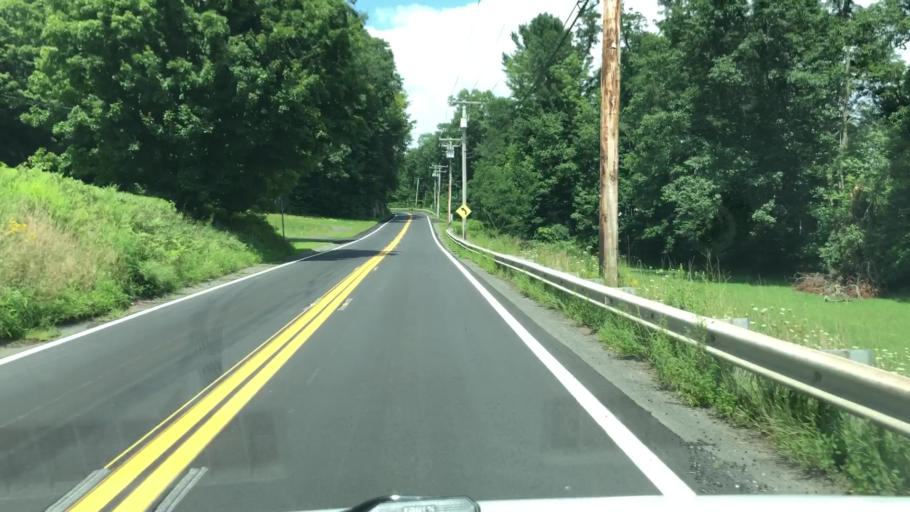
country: US
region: Massachusetts
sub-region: Franklin County
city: Ashfield
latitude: 42.5224
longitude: -72.7827
